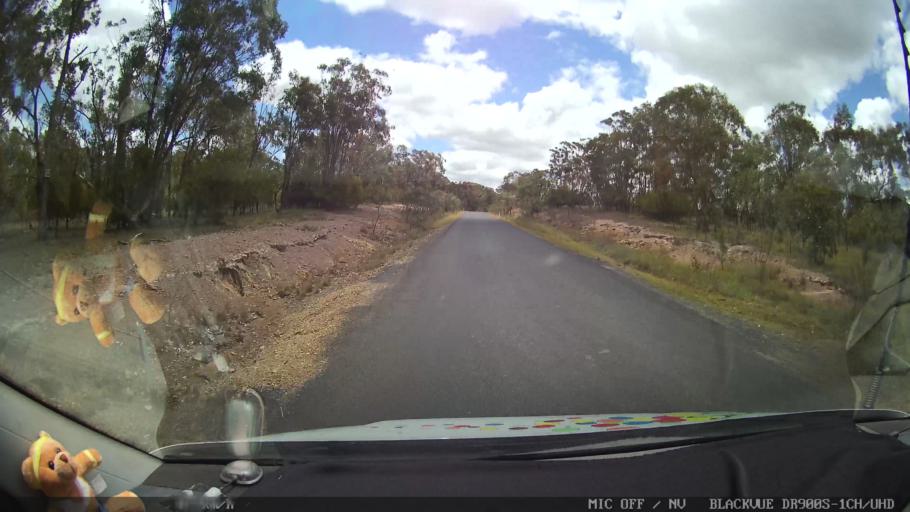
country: AU
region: New South Wales
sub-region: Glen Innes Severn
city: Glen Innes
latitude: -29.4307
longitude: 151.7913
